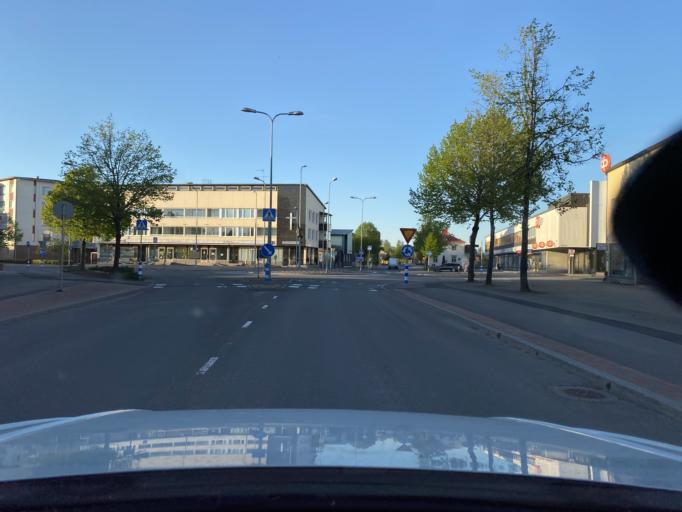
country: FI
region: Satakunta
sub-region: Pori
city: Huittinen
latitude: 61.1757
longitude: 22.6976
